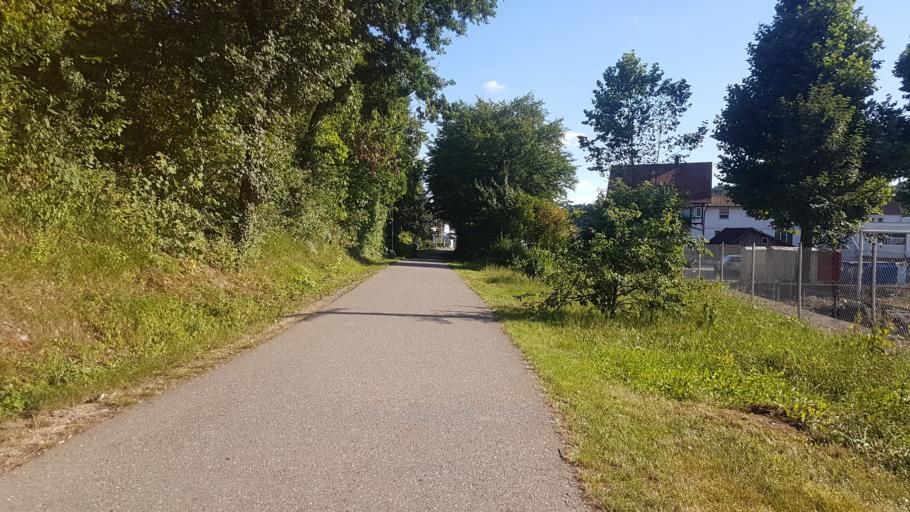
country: DE
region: Baden-Wuerttemberg
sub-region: Regierungsbezirk Stuttgart
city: Mockmuhl
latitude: 49.3229
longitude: 9.3653
